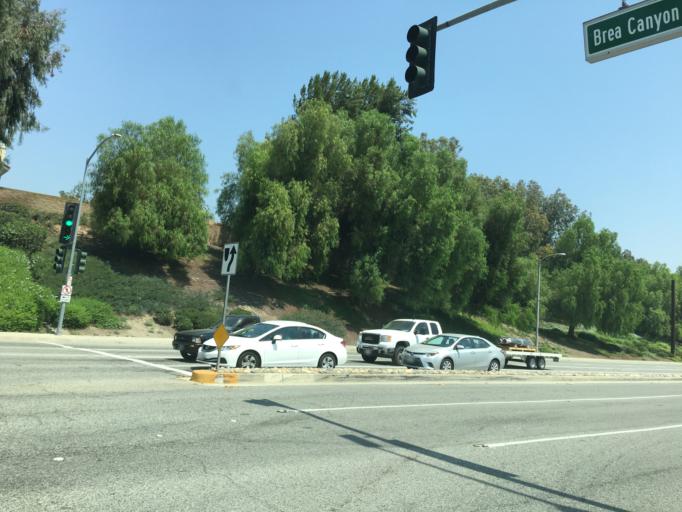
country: US
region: California
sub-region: Los Angeles County
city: Walnut
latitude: 34.0202
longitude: -117.8402
